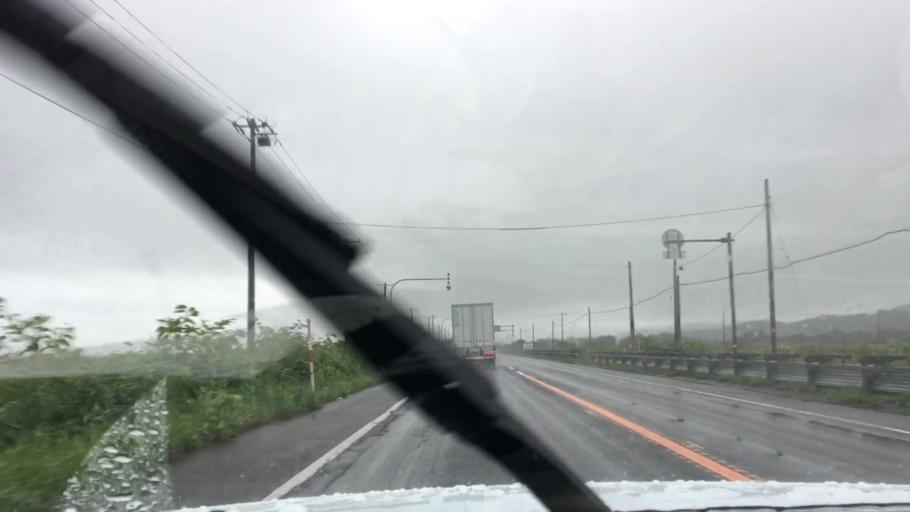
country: JP
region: Hokkaido
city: Niseko Town
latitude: 42.4268
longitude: 140.3166
